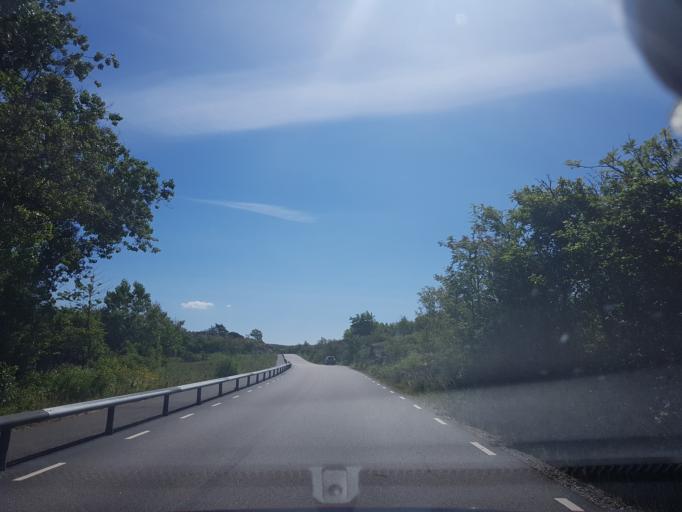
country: SE
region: Vaestra Goetaland
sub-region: Lysekils Kommun
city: Lysekil
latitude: 58.1682
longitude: 11.4176
